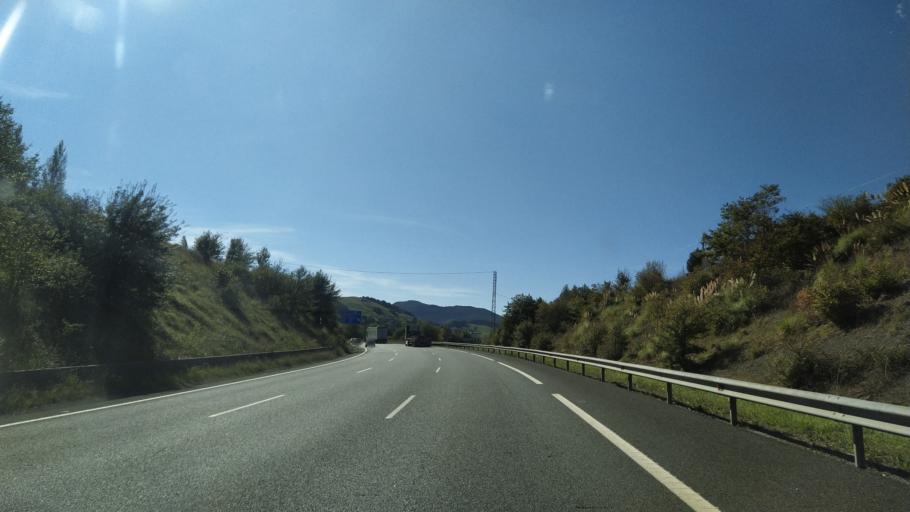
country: ES
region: Cantabria
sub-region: Provincia de Cantabria
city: Hazas de Cesto
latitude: 43.4169
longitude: -3.5540
